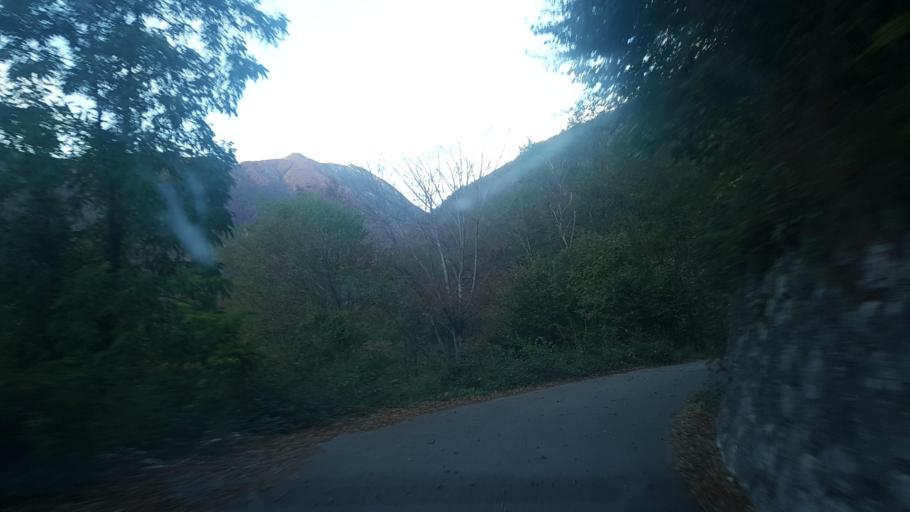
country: IT
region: Friuli Venezia Giulia
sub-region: Provincia di Udine
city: Preone
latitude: 46.3468
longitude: 12.8984
